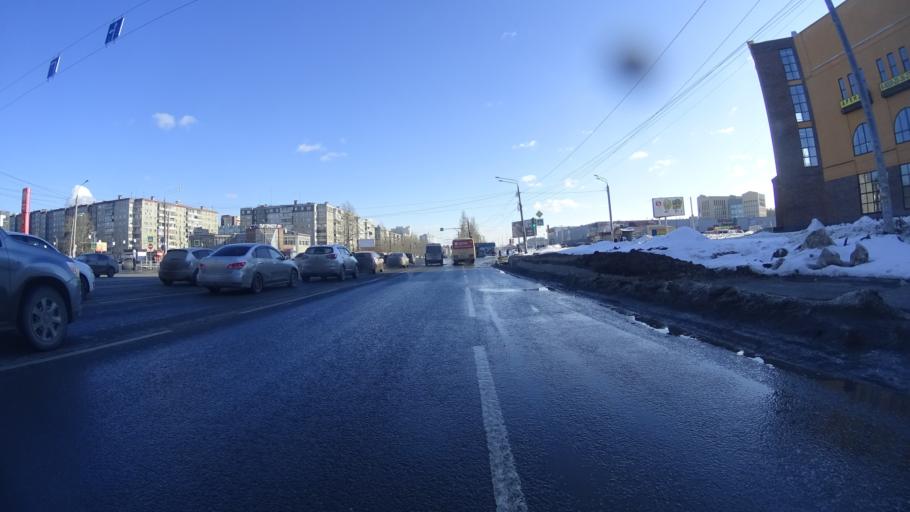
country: RU
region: Chelyabinsk
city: Roshchino
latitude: 55.1875
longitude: 61.2855
